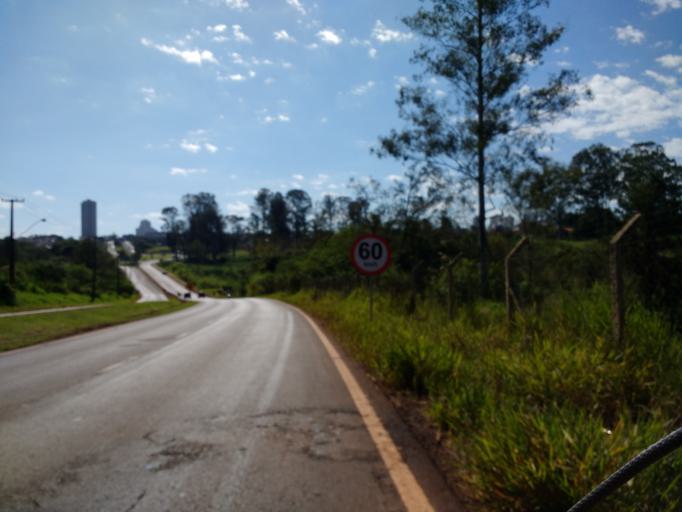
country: BR
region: Parana
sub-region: Londrina
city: Londrina
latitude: -23.3543
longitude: -51.1923
